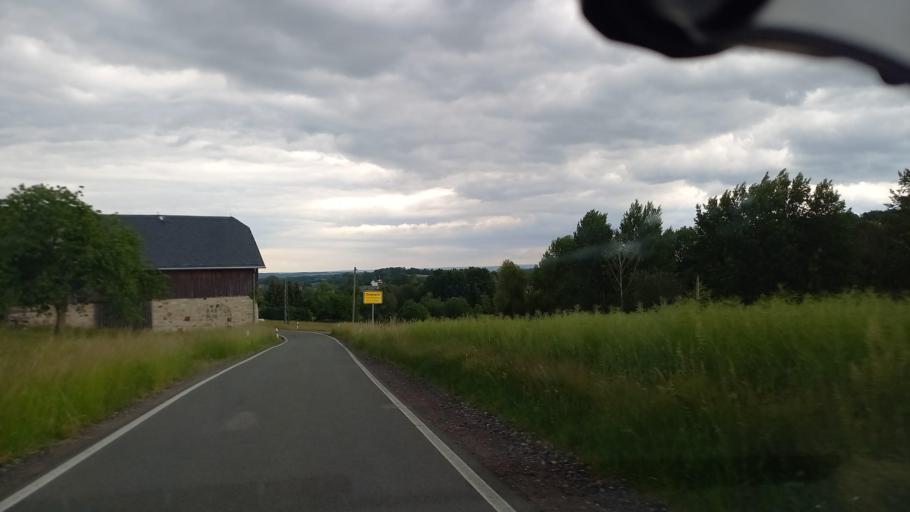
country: DE
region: Saxony
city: Rodewisch
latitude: 50.5715
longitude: 12.4439
